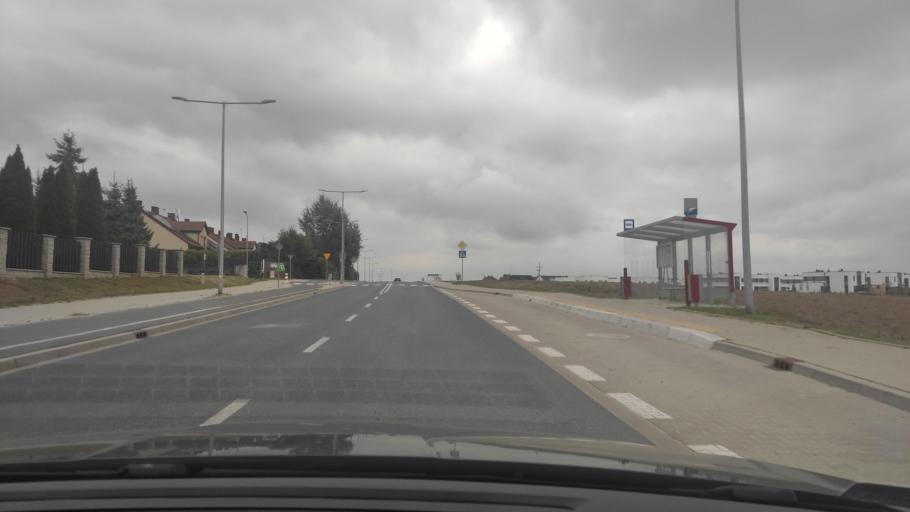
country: PL
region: Greater Poland Voivodeship
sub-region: Powiat poznanski
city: Swarzedz
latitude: 52.3832
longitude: 17.0612
